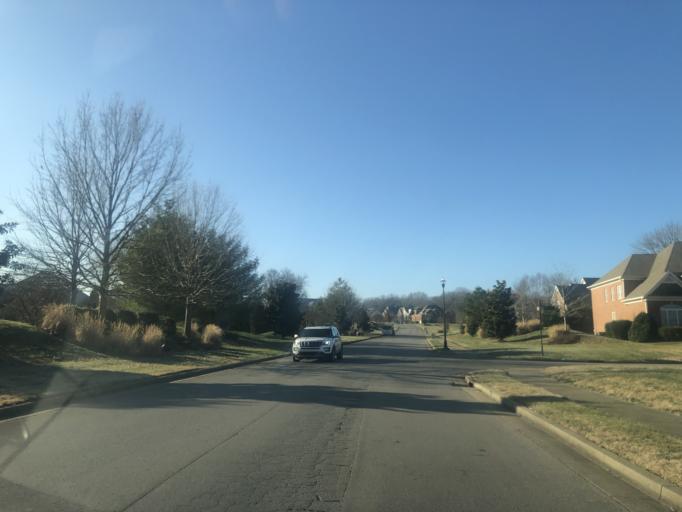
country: US
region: Tennessee
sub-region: Williamson County
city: Nolensville
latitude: 35.9635
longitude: -86.6925
